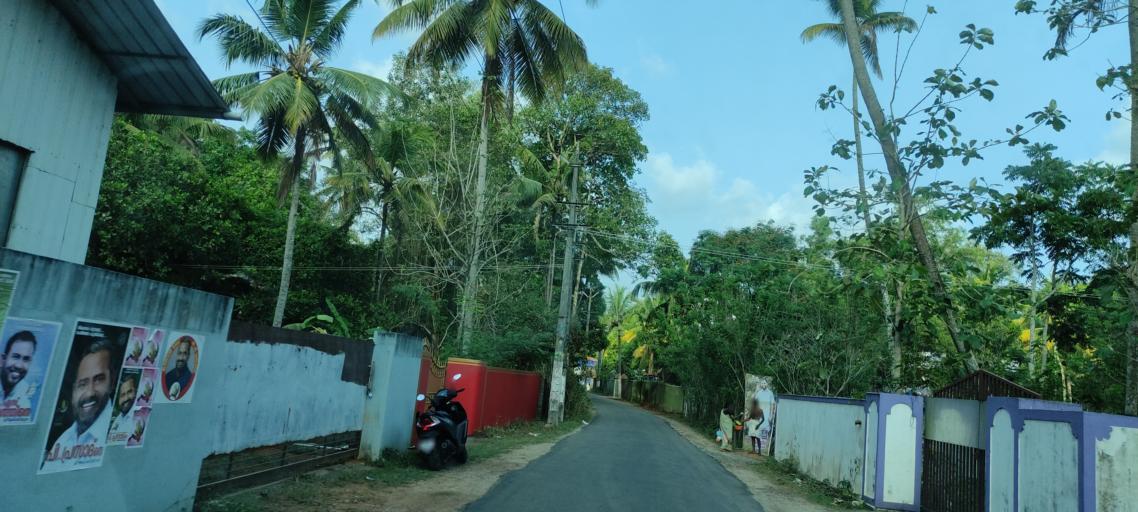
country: IN
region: Kerala
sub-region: Alappuzha
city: Vayalar
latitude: 9.7288
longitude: 76.3145
